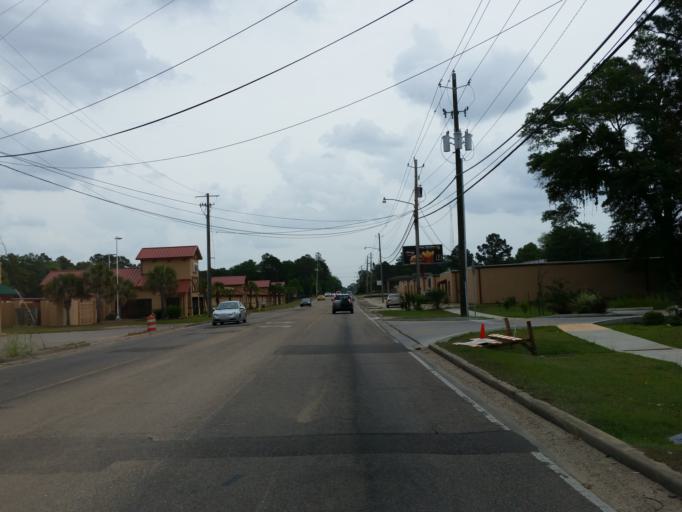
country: US
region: Mississippi
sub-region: Forrest County
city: Hattiesburg
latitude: 31.3041
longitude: -89.3297
